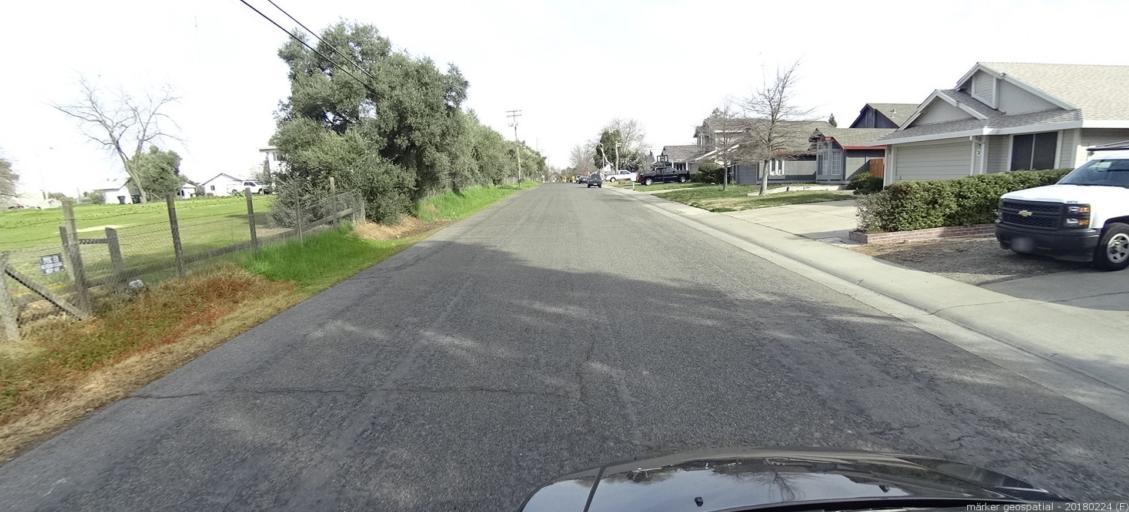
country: US
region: California
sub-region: Sacramento County
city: Rio Linda
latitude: 38.6921
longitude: -121.4615
